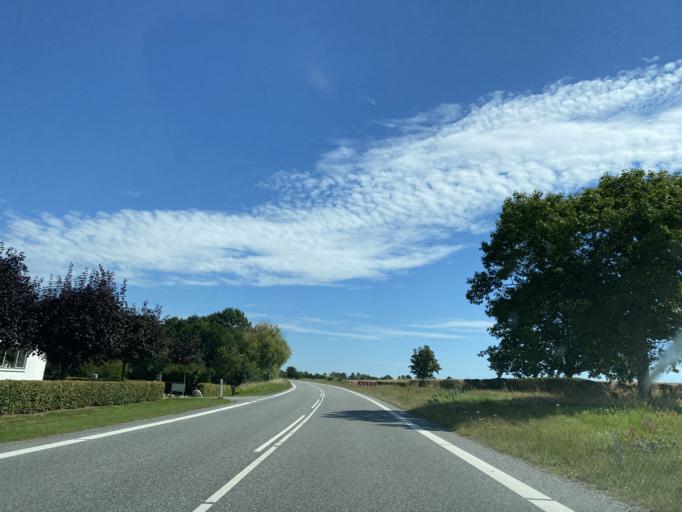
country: DK
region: South Denmark
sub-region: Faaborg-Midtfyn Kommune
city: Faaborg
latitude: 55.1087
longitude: 10.1971
